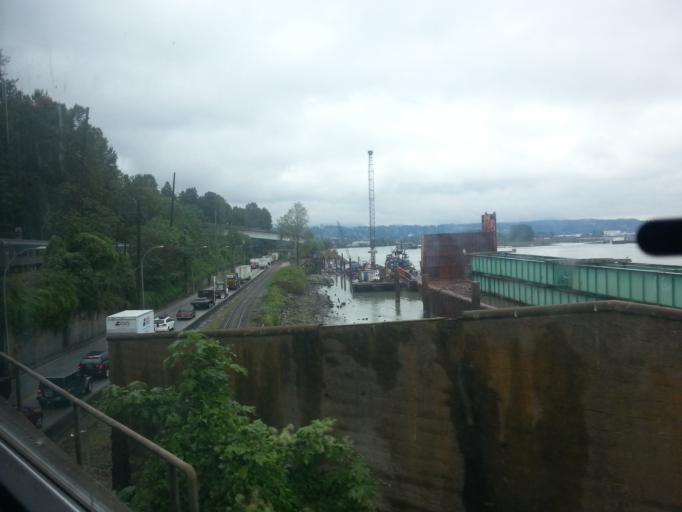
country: CA
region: British Columbia
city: New Westminster
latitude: 49.2096
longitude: -122.8971
